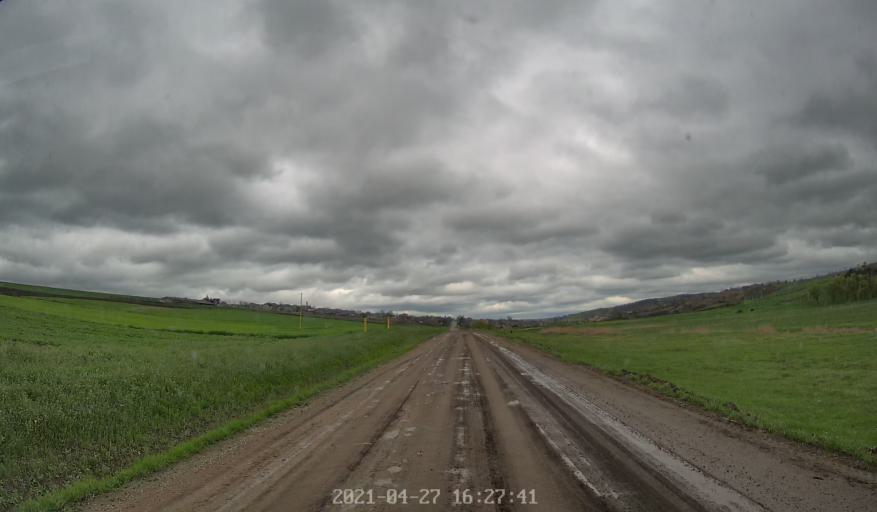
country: MD
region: Chisinau
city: Singera
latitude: 46.9746
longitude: 29.0359
